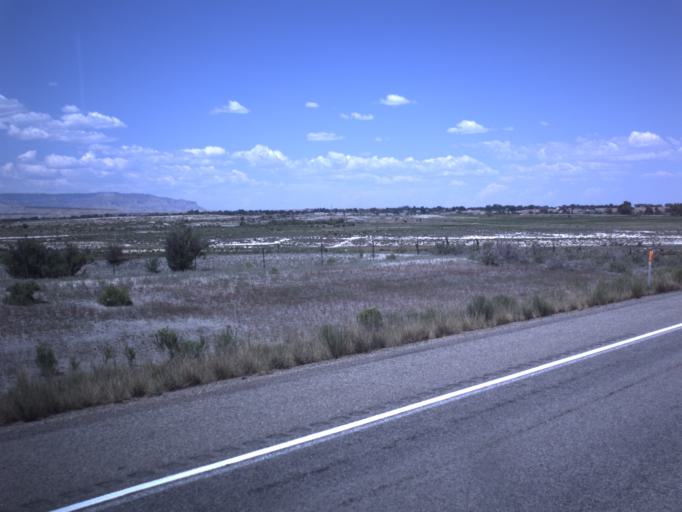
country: US
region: Utah
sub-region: Emery County
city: Castle Dale
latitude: 39.1868
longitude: -111.0307
